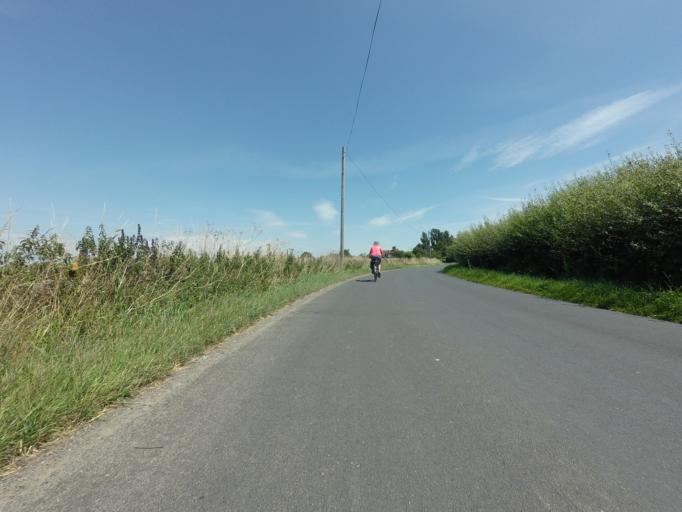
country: GB
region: England
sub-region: Kent
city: Lydd
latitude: 50.9882
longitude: 0.8898
